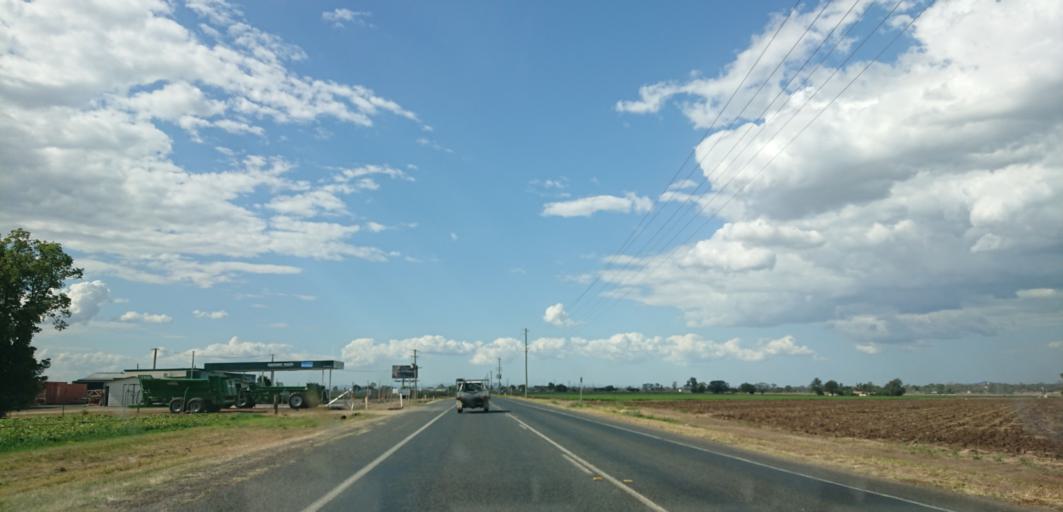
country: AU
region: Queensland
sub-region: Lockyer Valley
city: Gatton
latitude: -27.5536
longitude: 152.3072
